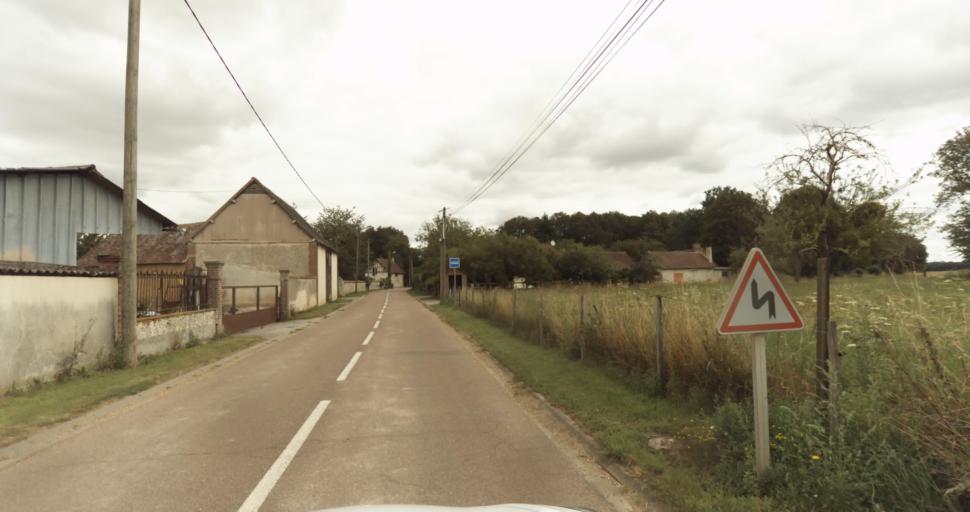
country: FR
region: Haute-Normandie
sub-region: Departement de l'Eure
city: La Madeleine-de-Nonancourt
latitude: 48.8117
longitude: 1.2149
